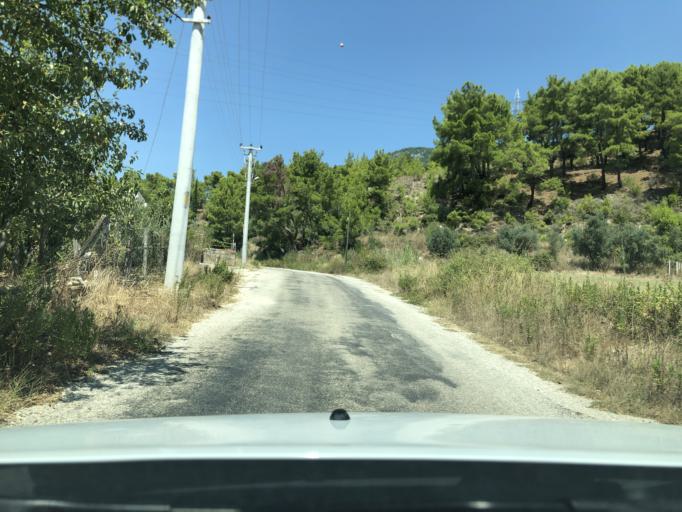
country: TR
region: Antalya
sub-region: Manavgat
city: Kizilagac
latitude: 36.8619
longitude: 31.5642
